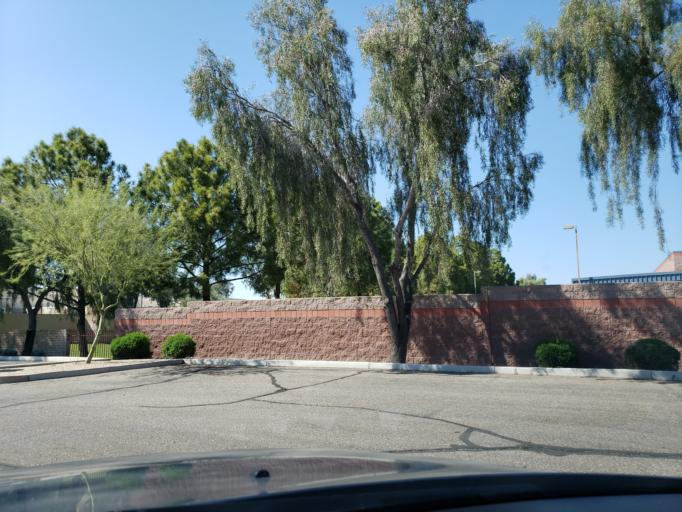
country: US
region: Arizona
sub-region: Maricopa County
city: Glendale
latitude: 33.5799
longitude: -112.1881
